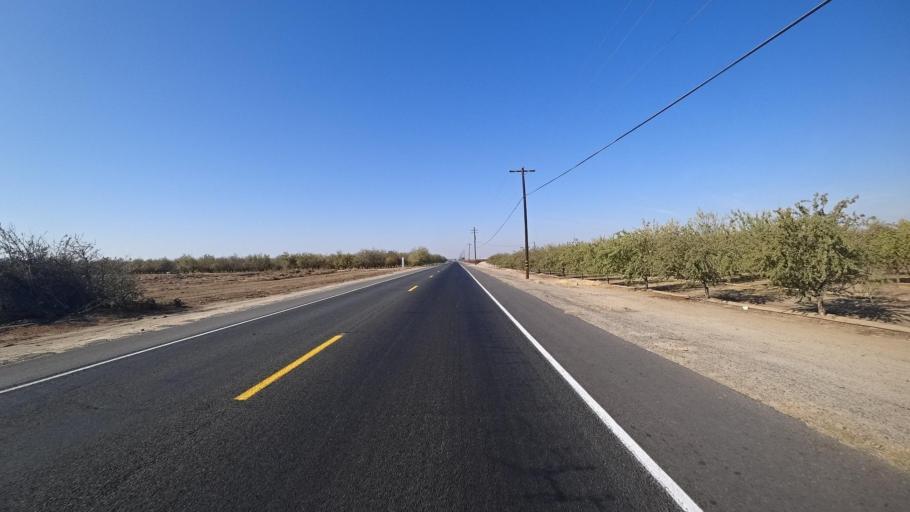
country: US
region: California
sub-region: Kern County
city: Delano
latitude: 35.7178
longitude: -119.2796
